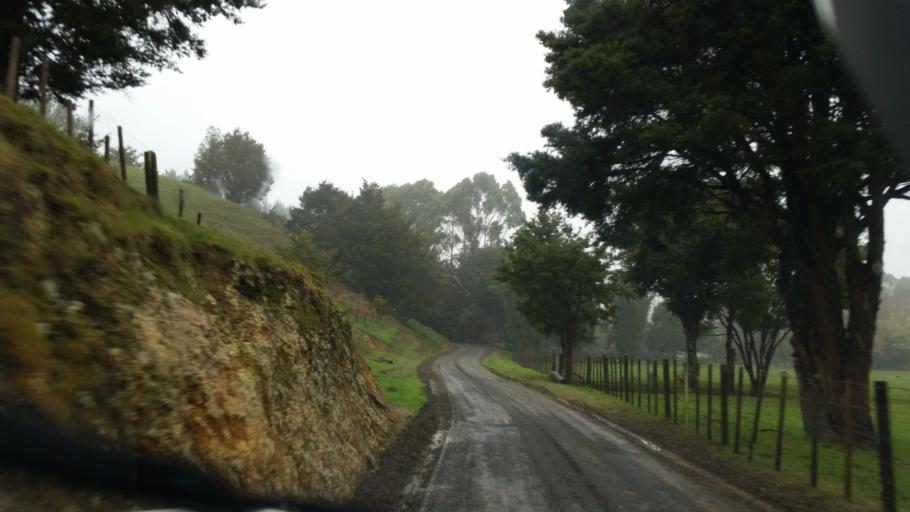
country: NZ
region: Northland
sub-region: Whangarei
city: Ngunguru
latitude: -35.4925
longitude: 174.4255
